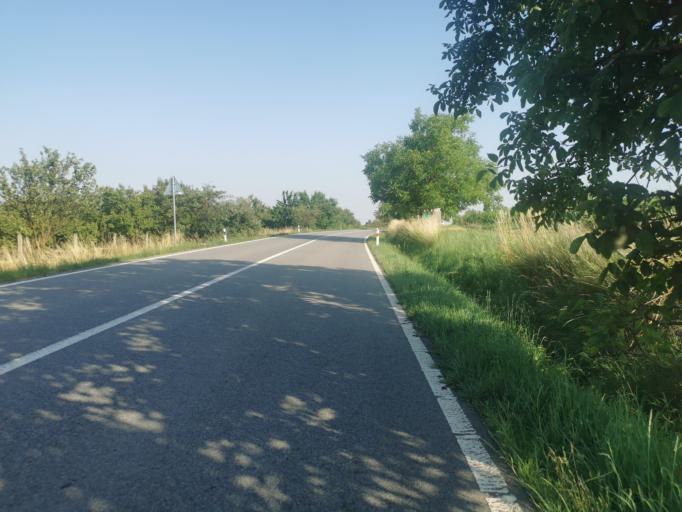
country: CZ
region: South Moravian
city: Milotice
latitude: 48.9391
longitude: 17.1533
